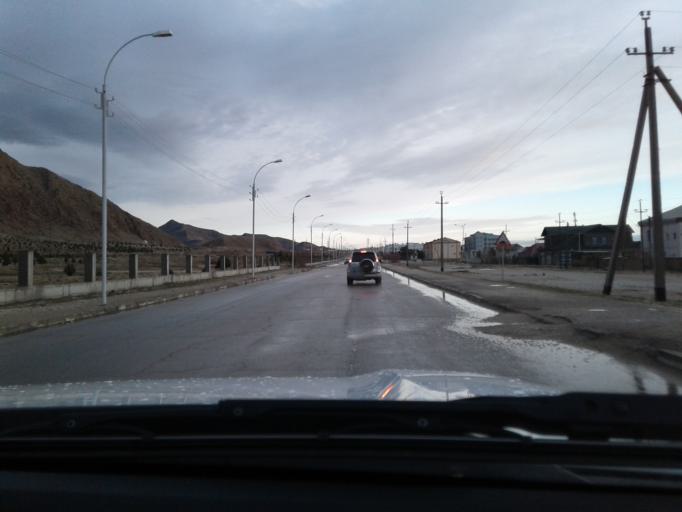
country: TM
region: Balkan
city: Balkanabat
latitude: 39.5287
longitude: 54.3596
